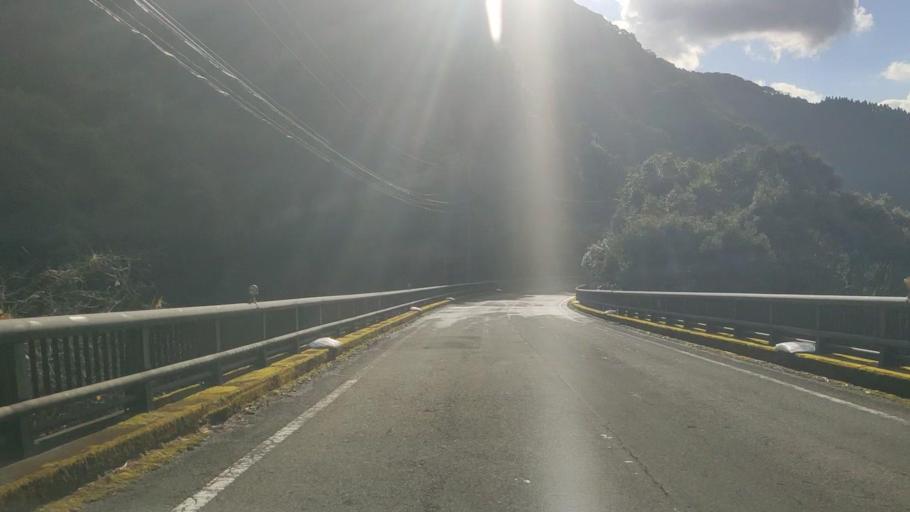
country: JP
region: Kumamoto
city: Hitoyoshi
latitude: 32.3795
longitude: 130.8376
